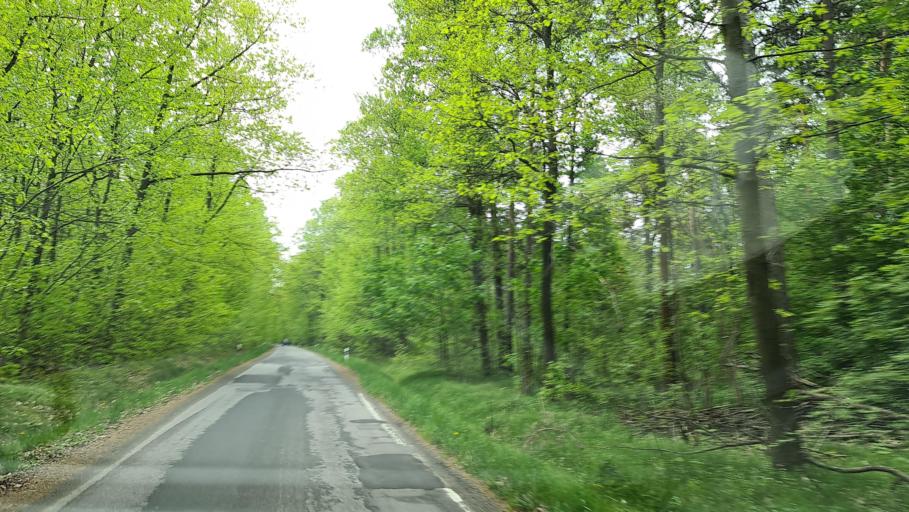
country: DE
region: Saxony
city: Hilbersdorf
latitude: 50.8454
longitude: 12.9858
